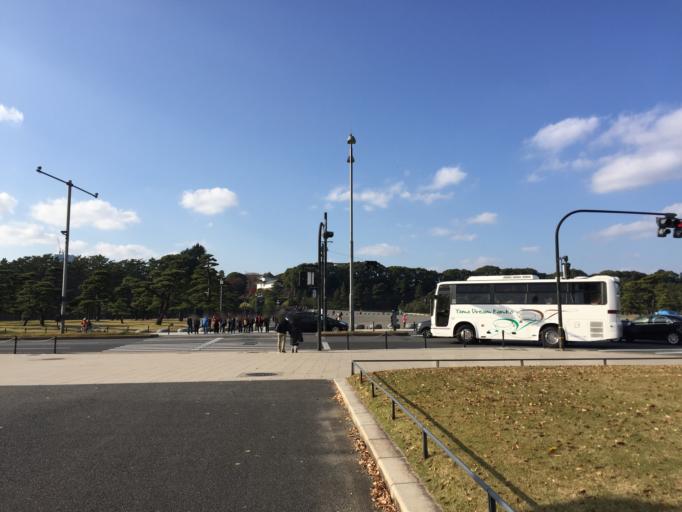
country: JP
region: Tokyo
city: Tokyo
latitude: 35.6792
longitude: 139.7579
